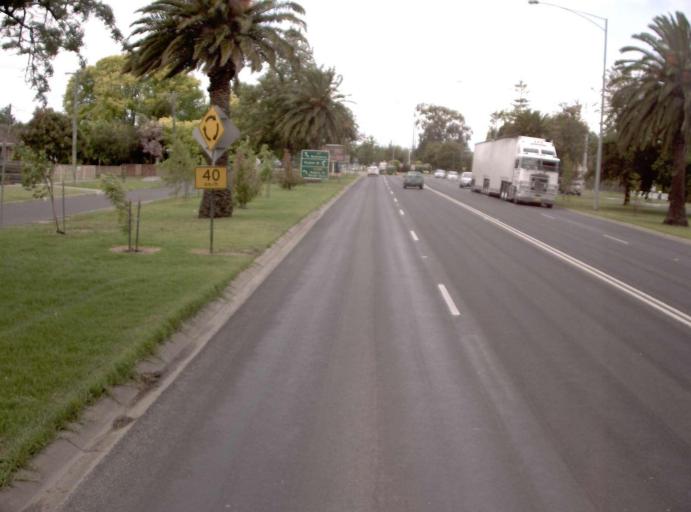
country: AU
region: Victoria
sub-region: Wellington
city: Sale
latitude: -38.0966
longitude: 147.0683
